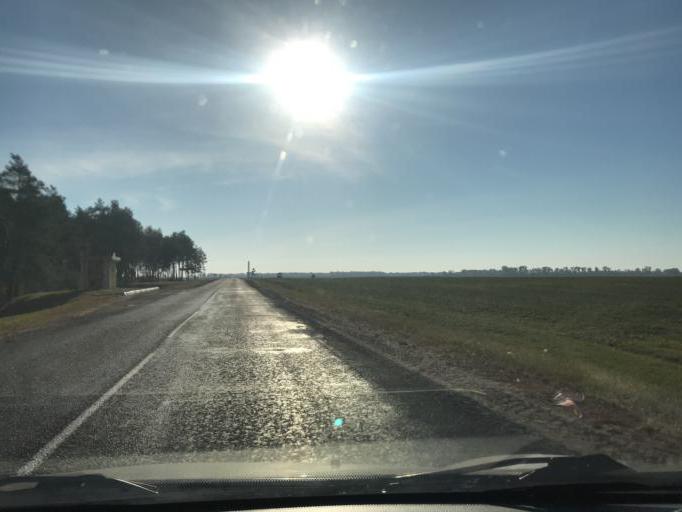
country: BY
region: Gomel
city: Khoyniki
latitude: 51.8132
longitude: 30.0984
